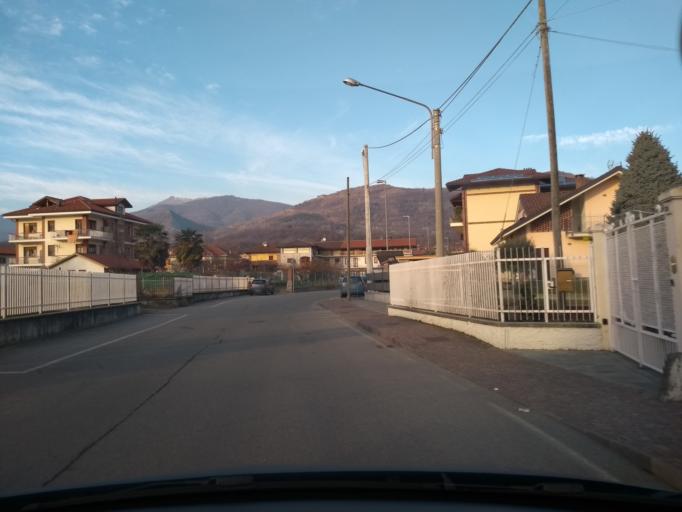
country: IT
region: Piedmont
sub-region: Provincia di Torino
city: Balangero
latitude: 45.2707
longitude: 7.5175
